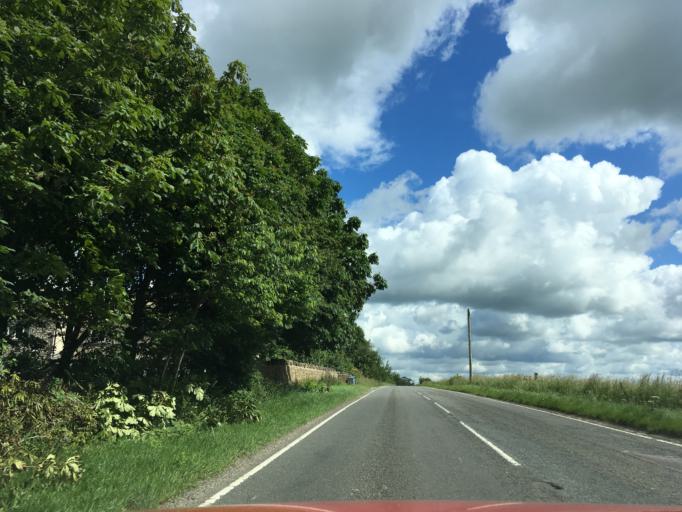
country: GB
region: England
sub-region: Oxfordshire
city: Shipton under Wychwood
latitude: 51.8322
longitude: -1.6087
